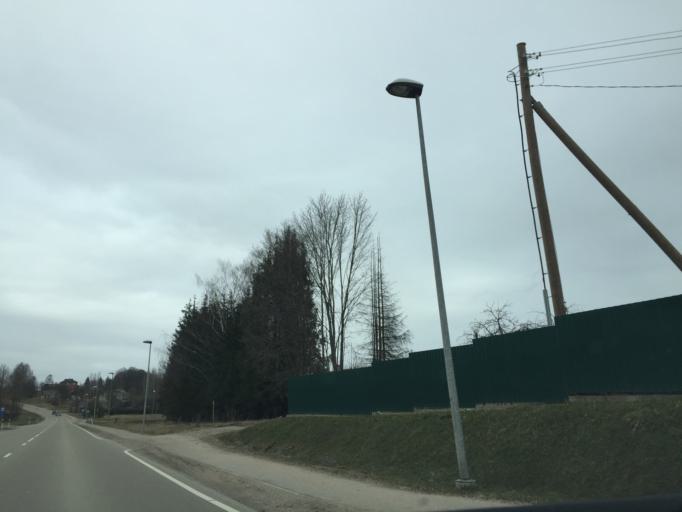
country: LV
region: Kraslavas Rajons
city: Kraslava
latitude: 55.9071
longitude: 27.1546
